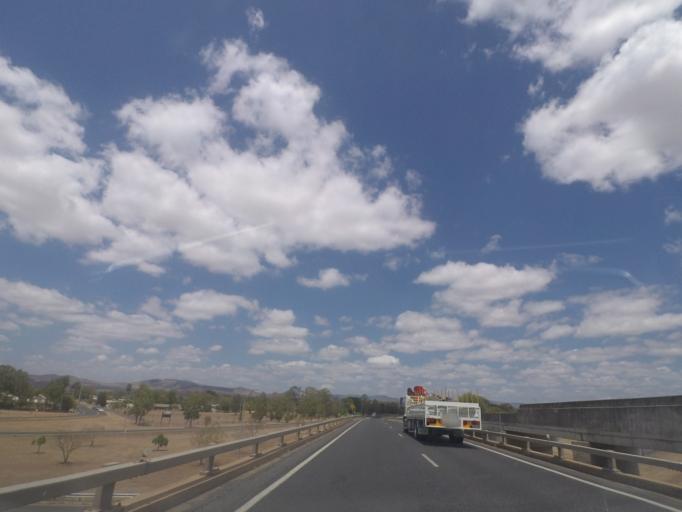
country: AU
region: Queensland
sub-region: Lockyer Valley
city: Gatton
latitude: -27.5526
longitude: 152.1298
